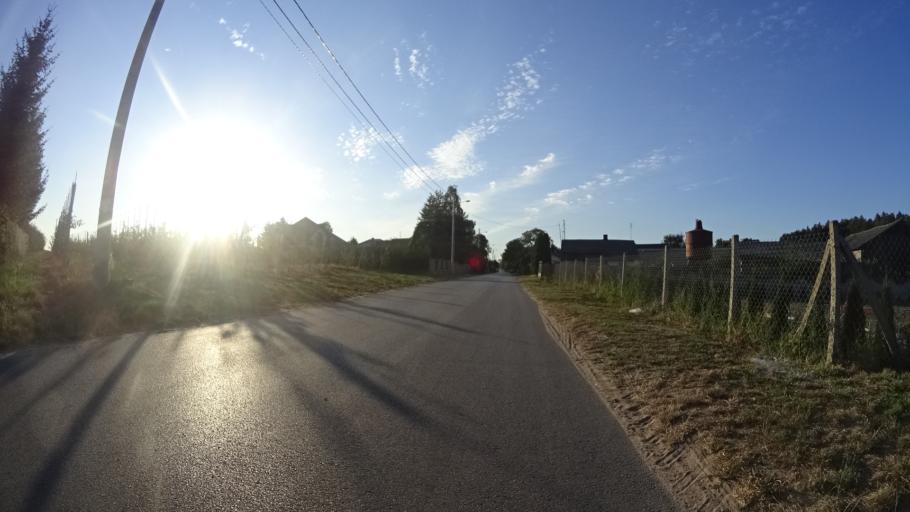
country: PL
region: Masovian Voivodeship
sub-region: Powiat grojecki
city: Goszczyn
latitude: 51.6954
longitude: 20.8134
